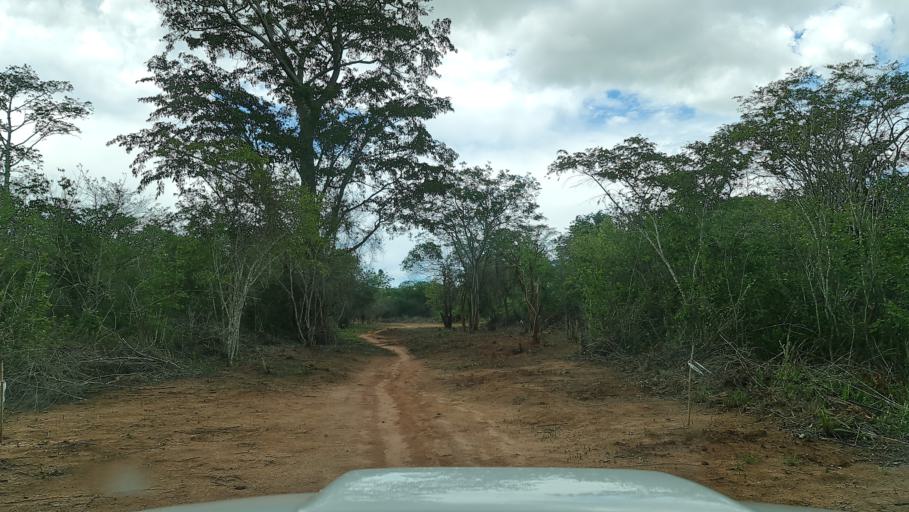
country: MZ
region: Nampula
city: Ilha de Mocambique
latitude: -15.5007
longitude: 40.1798
